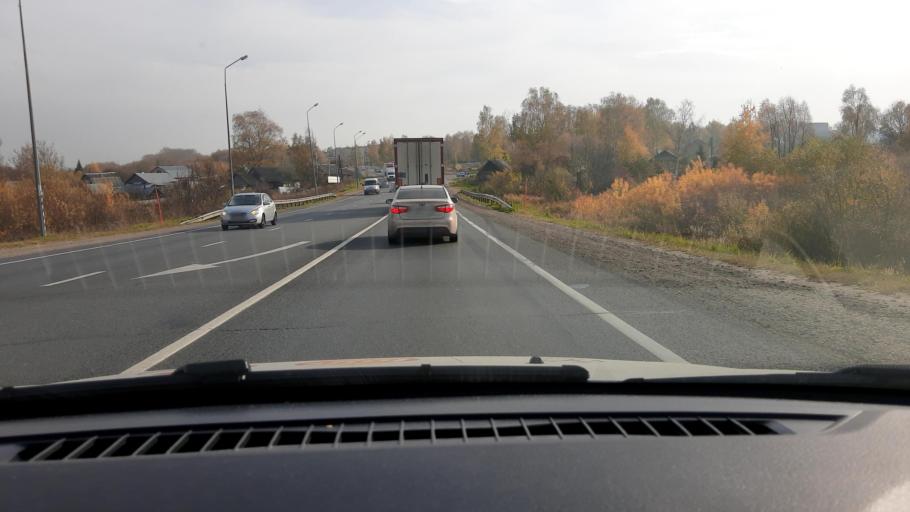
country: RU
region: Nizjnij Novgorod
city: Pamyat' Parizhskoy Kommuny
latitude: 56.0443
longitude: 44.4382
